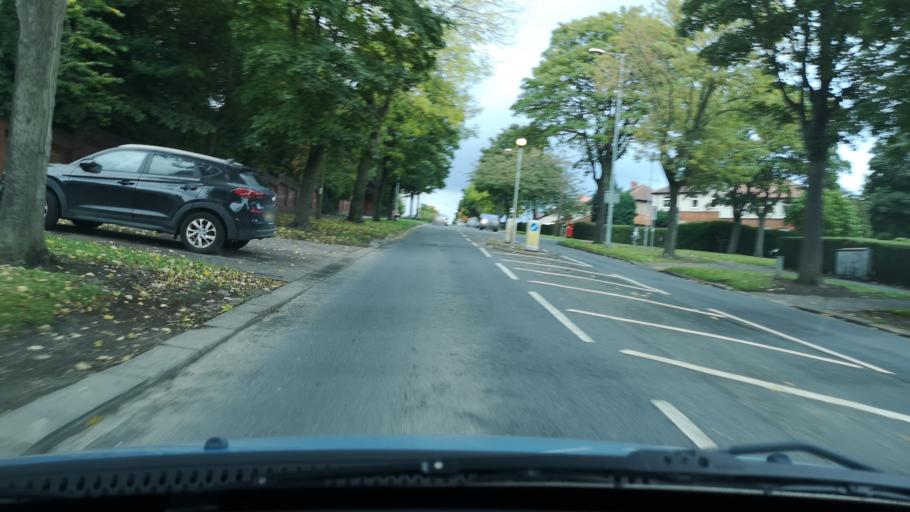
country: GB
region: England
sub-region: City and Borough of Wakefield
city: Horbury
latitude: 53.6742
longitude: -1.5393
